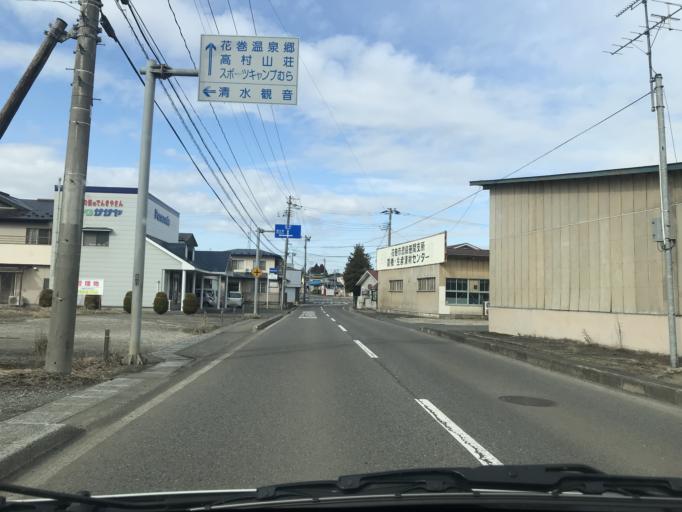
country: JP
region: Iwate
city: Hanamaki
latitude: 39.3600
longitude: 141.0507
